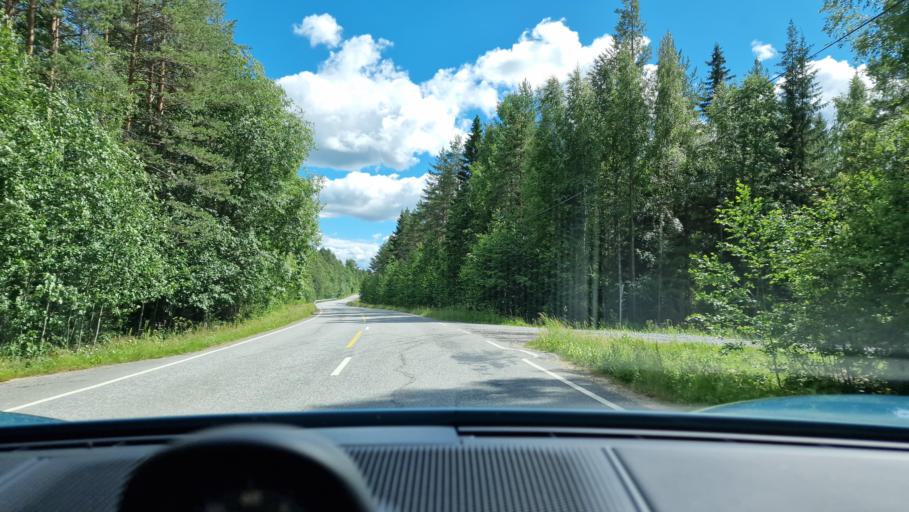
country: FI
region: Southern Ostrobothnia
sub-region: Jaerviseutu
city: Soini
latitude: 62.8241
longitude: 24.3433
